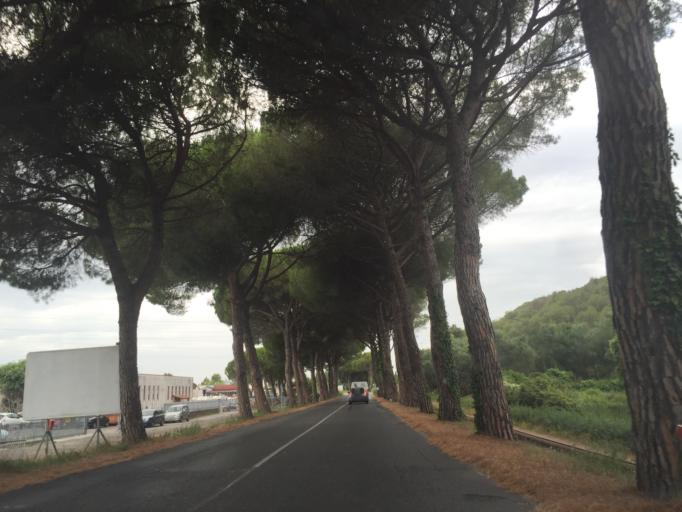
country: IT
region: Tuscany
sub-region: Province of Pisa
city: Uliveto Terme
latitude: 43.6881
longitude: 10.5387
